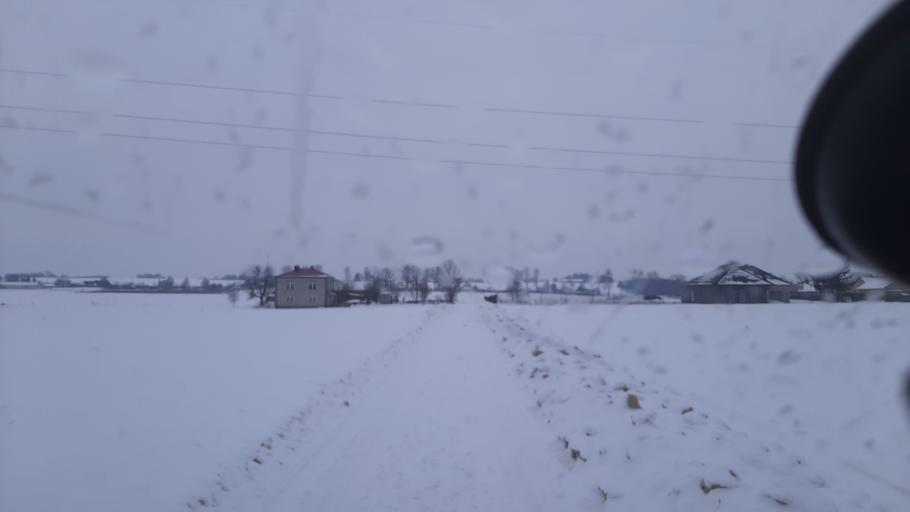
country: PL
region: Lublin Voivodeship
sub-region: Powiat lubelski
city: Jastkow
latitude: 51.3512
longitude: 22.4004
